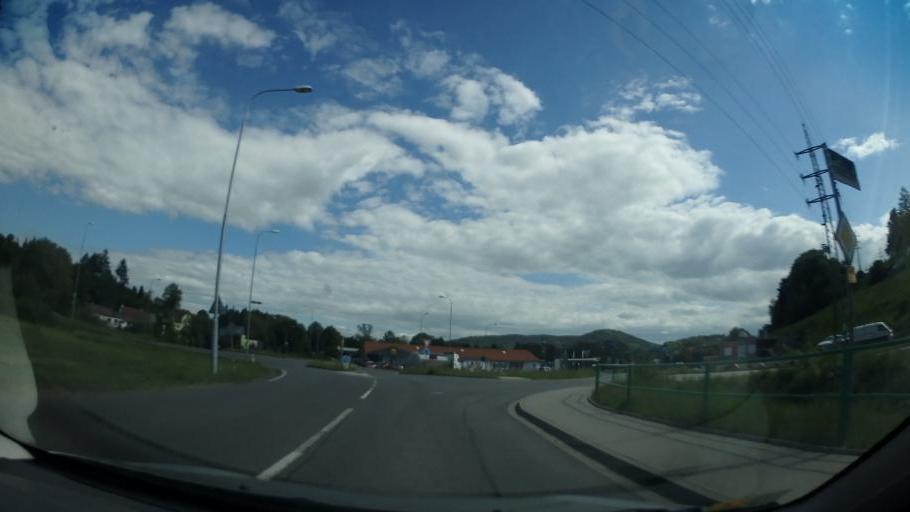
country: CZ
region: Pardubicky
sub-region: Okres Svitavy
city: Moravska Trebova
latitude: 49.7499
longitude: 16.6570
